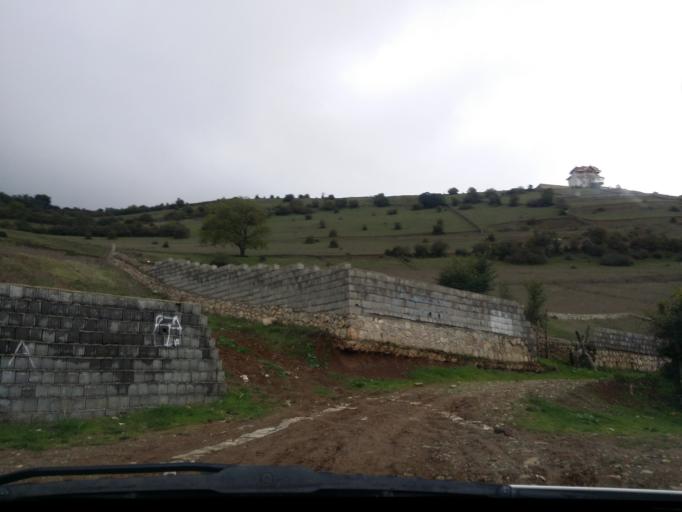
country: IR
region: Mazandaran
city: `Abbasabad
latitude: 36.5031
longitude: 51.1839
